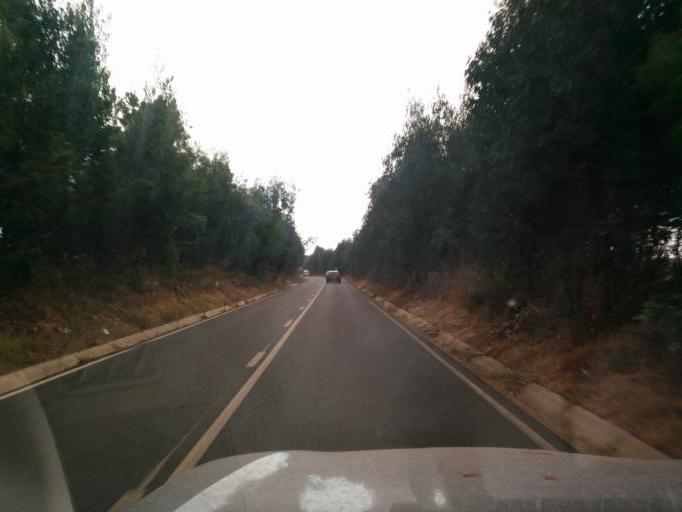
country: PT
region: Beja
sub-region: Odemira
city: Sao Teotonio
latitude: 37.5844
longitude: -8.7389
